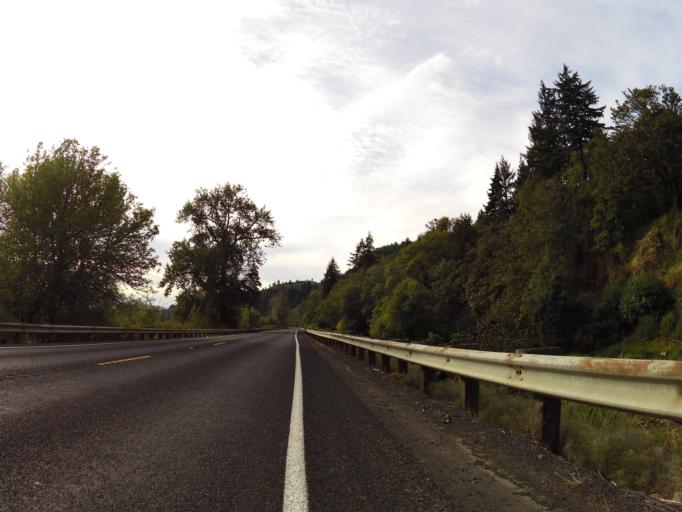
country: US
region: Washington
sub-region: Cowlitz County
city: West Longview
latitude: 46.1845
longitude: -123.0797
